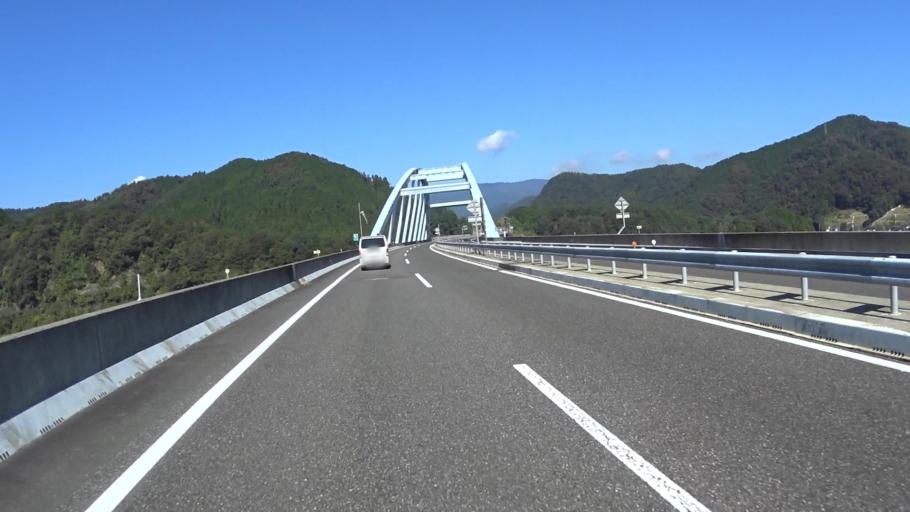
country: JP
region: Kyoto
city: Miyazu
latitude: 35.4212
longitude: 135.2130
